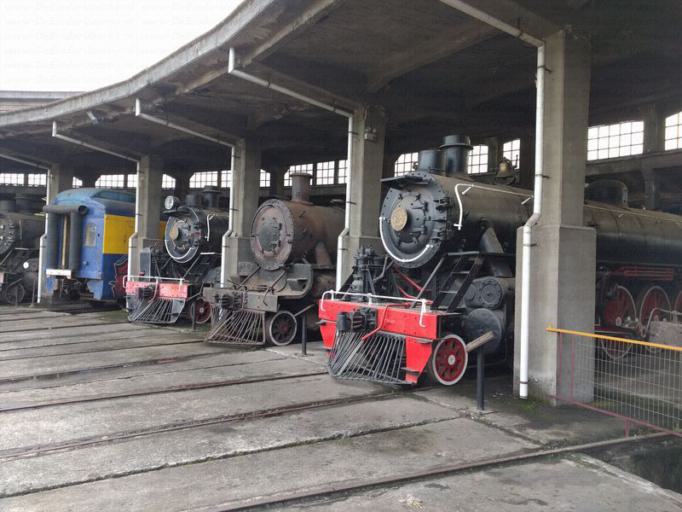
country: CL
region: Araucania
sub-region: Provincia de Cautin
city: Temuco
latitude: -38.7257
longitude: -72.5709
